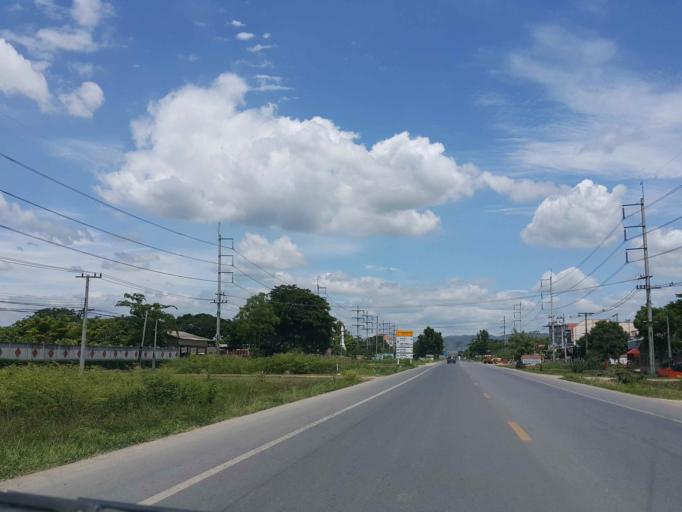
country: TH
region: Chiang Mai
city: Hang Dong
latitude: 18.7221
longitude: 98.9541
